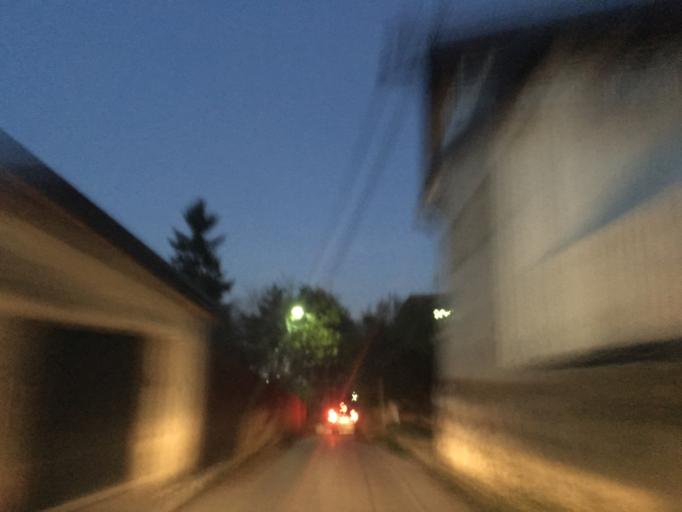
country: BA
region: Federation of Bosnia and Herzegovina
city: Kobilja Glava
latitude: 43.8486
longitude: 18.4128
